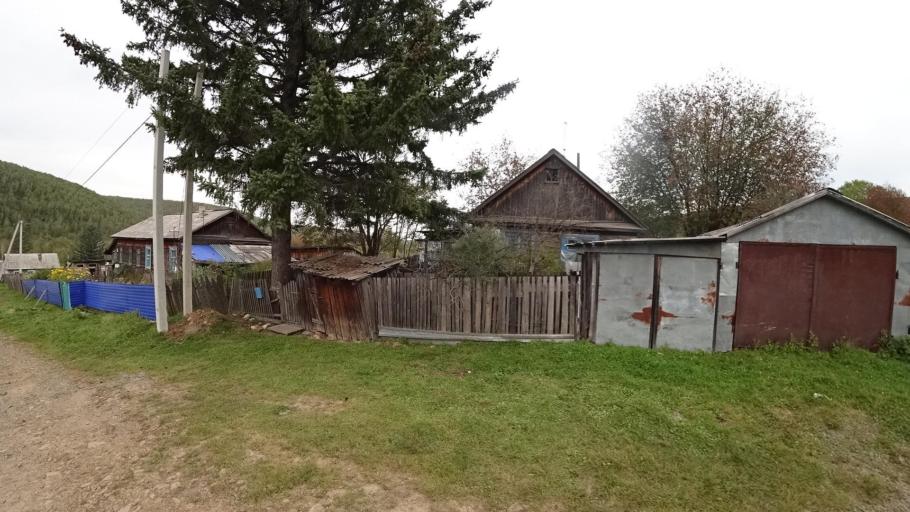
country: RU
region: Jewish Autonomous Oblast
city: Khingansk
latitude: 49.1298
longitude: 131.2014
